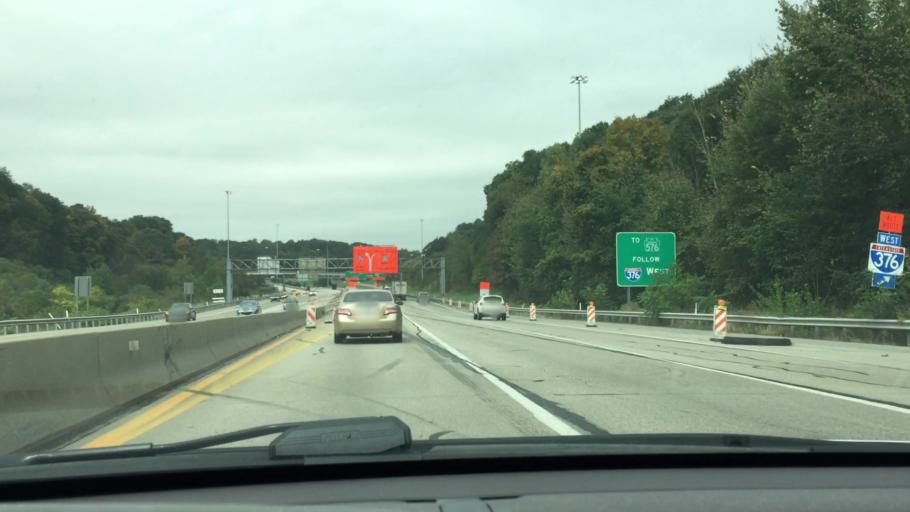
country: US
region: Pennsylvania
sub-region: Allegheny County
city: Enlow
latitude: 40.4619
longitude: -80.1928
